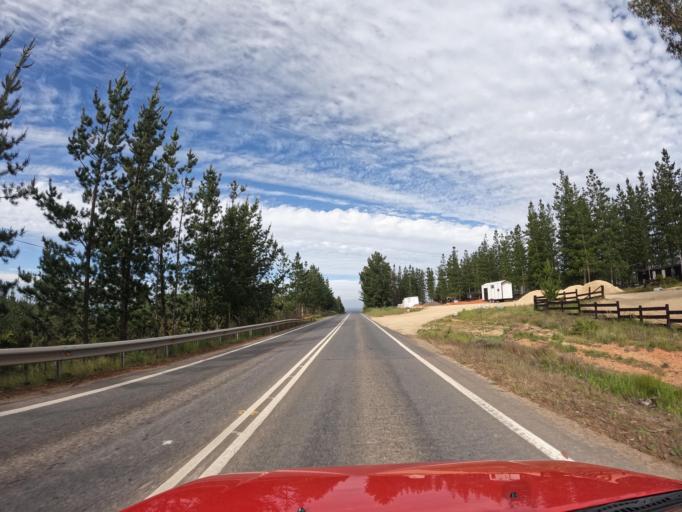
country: CL
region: O'Higgins
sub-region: Provincia de Colchagua
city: Santa Cruz
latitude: -34.3102
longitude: -71.8432
